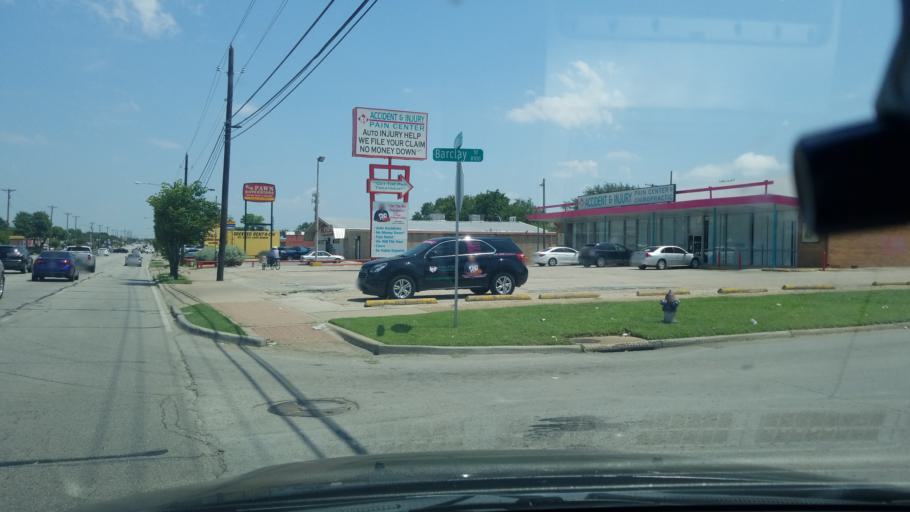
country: US
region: Texas
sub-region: Dallas County
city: Balch Springs
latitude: 32.7500
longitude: -96.6828
